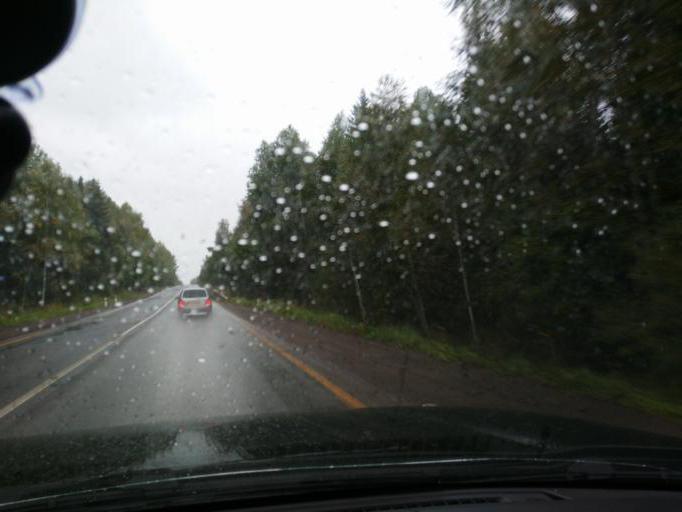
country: RU
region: Perm
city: Barda
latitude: 56.8961
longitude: 55.7321
